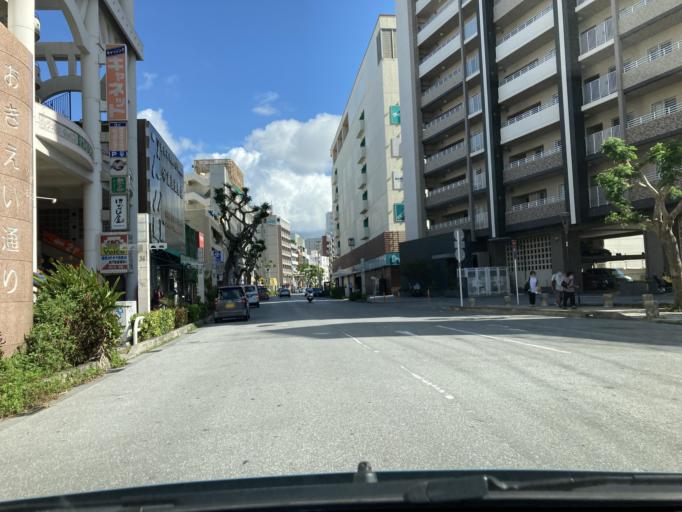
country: JP
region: Okinawa
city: Naha-shi
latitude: 26.2193
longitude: 127.6852
